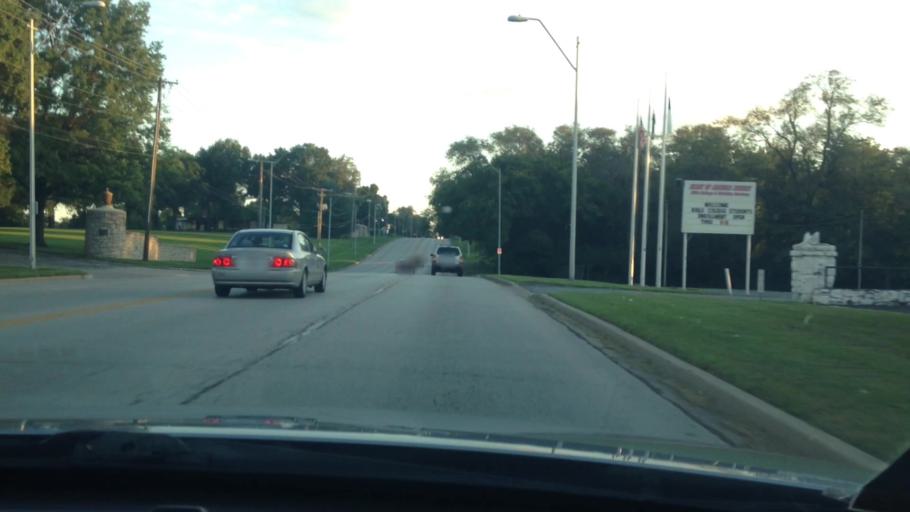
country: US
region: Missouri
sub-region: Jackson County
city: Raytown
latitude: 38.9871
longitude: -94.4831
